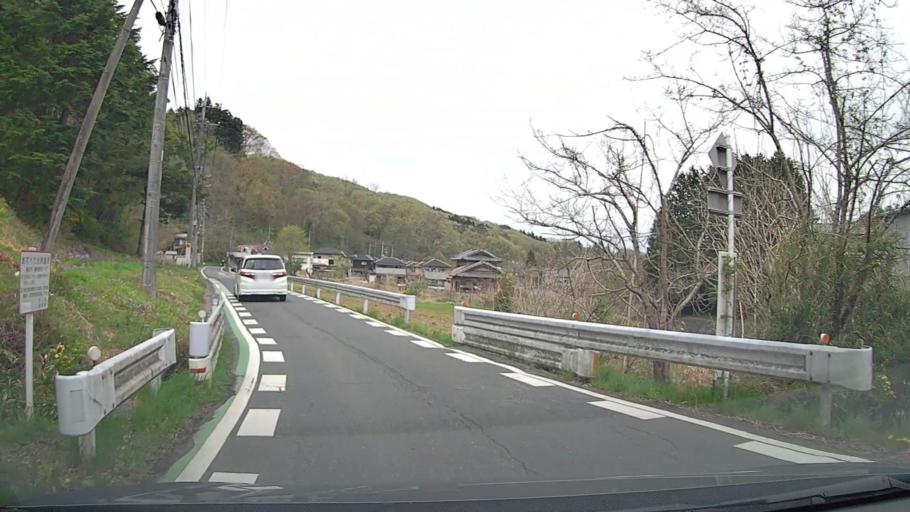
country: JP
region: Saitama
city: Chichibu
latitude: 36.0512
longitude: 139.1320
